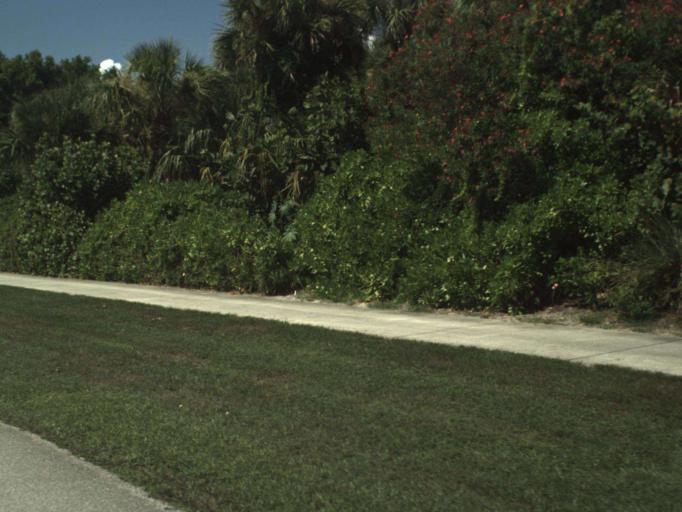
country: US
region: Florida
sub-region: Indian River County
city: Indian River Shores
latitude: 27.7187
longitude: -80.3784
